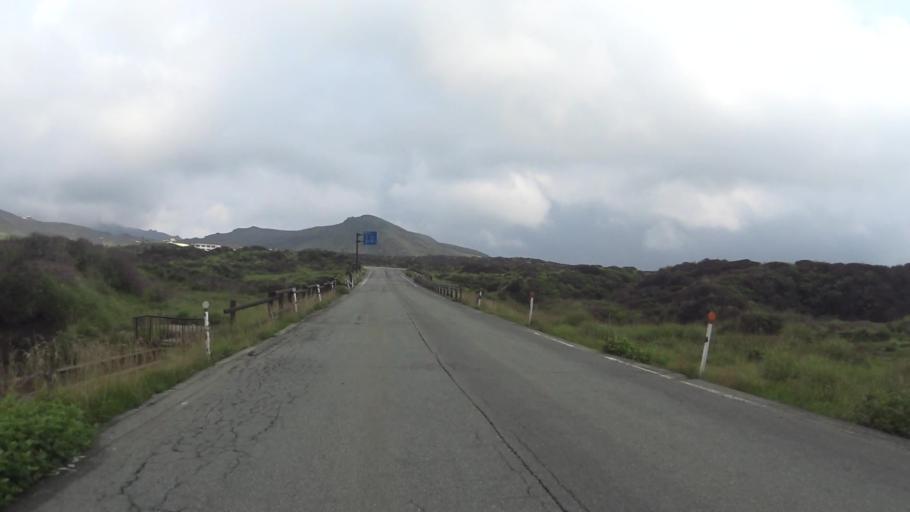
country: JP
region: Kumamoto
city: Aso
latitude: 32.8832
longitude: 131.0659
